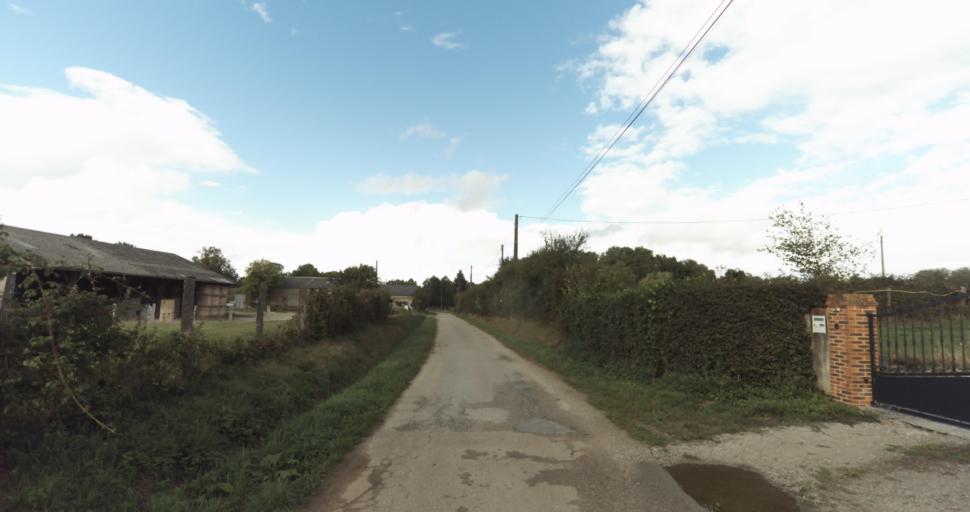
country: FR
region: Lower Normandy
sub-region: Departement de l'Orne
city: Sainte-Gauburge-Sainte-Colombe
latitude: 48.7555
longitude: 0.4015
